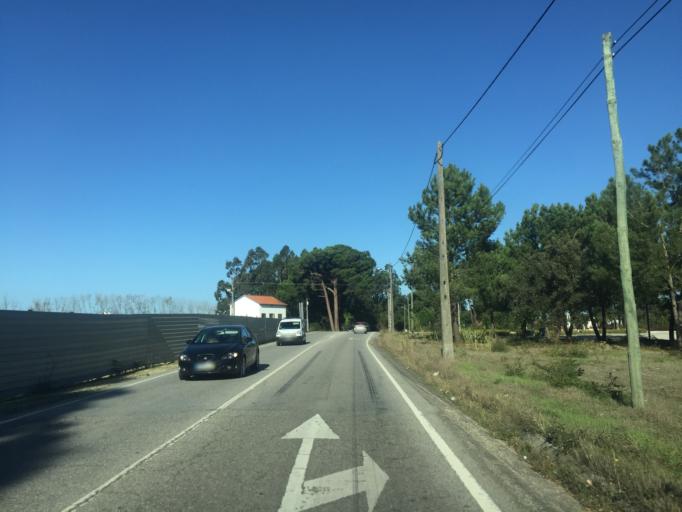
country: PT
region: Leiria
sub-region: Leiria
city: Amor
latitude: 39.7940
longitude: -8.8335
